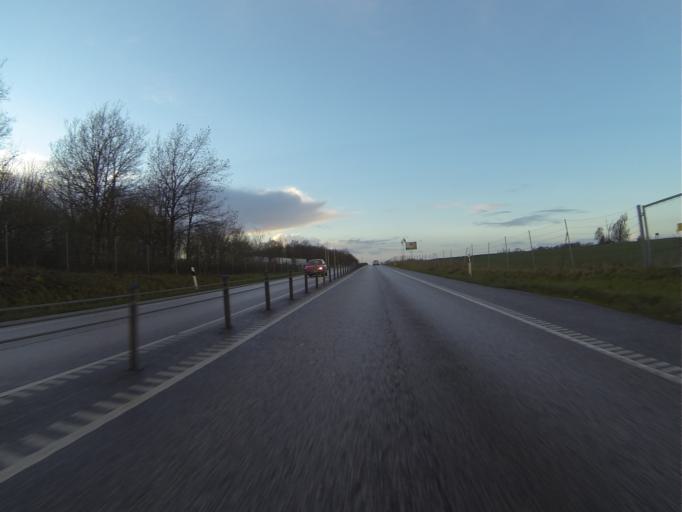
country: SE
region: Skane
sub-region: Svedala Kommun
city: Svedala
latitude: 55.5114
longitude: 13.3119
